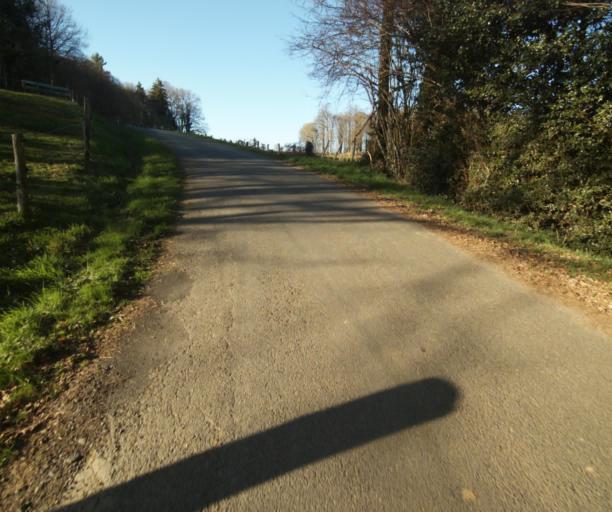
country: FR
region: Limousin
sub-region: Departement de la Correze
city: Seilhac
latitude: 45.3574
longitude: 1.7006
